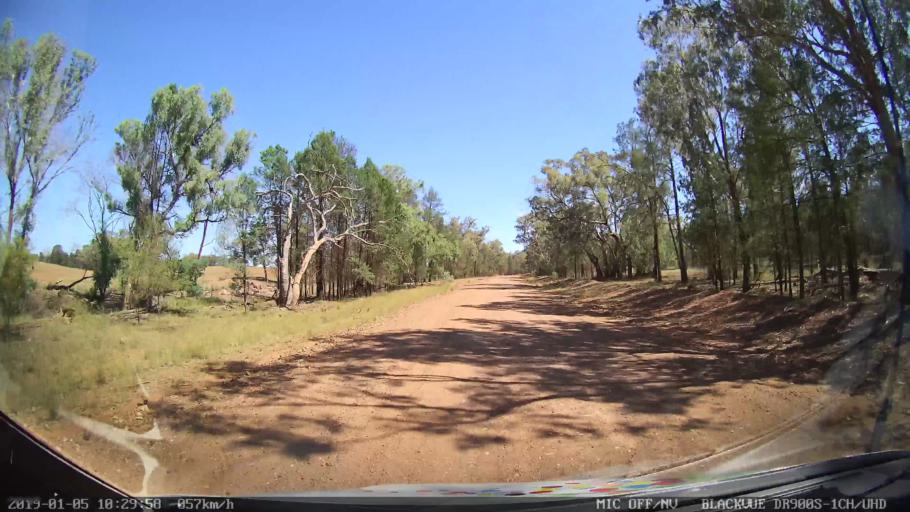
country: AU
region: New South Wales
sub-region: Gilgandra
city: Gilgandra
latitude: -31.5365
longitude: 148.9259
